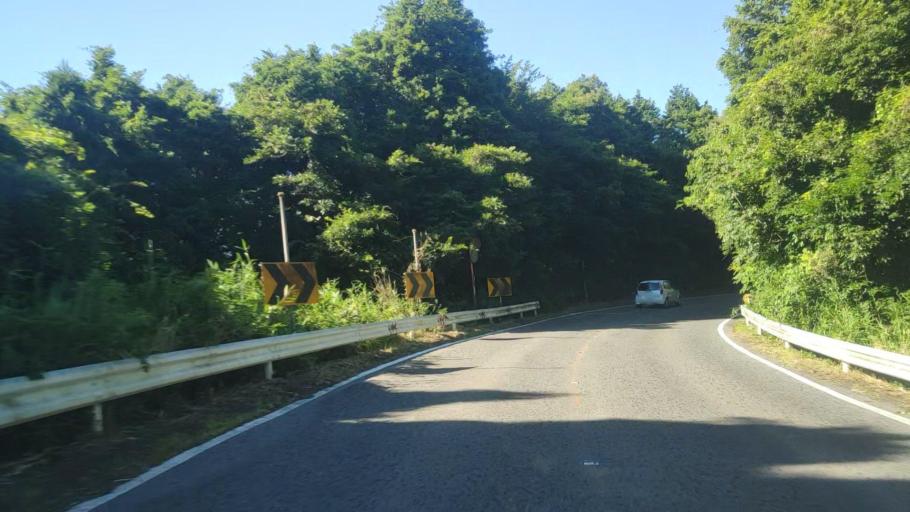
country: JP
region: Mie
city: Ueno-ebisumachi
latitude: 34.8458
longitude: 136.2367
